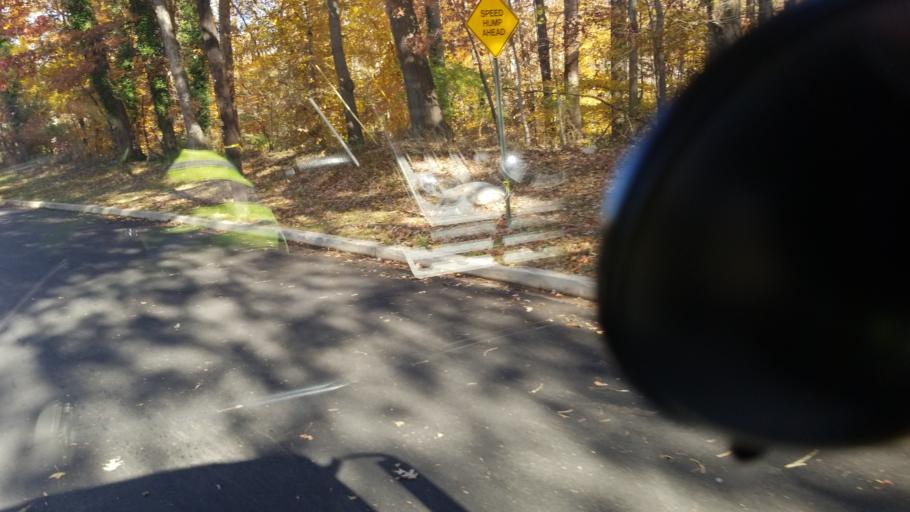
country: US
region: Maryland
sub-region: Prince George's County
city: Coral Hills
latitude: 38.8850
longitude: -76.9452
